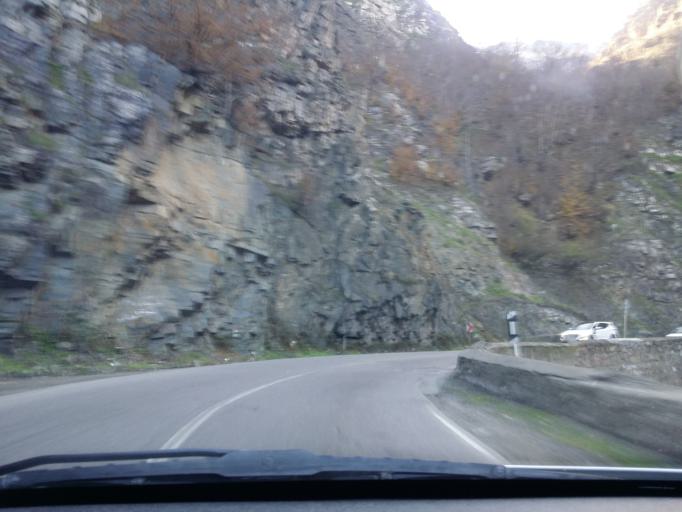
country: IR
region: Mazandaran
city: Chalus
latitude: 36.2810
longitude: 51.2434
